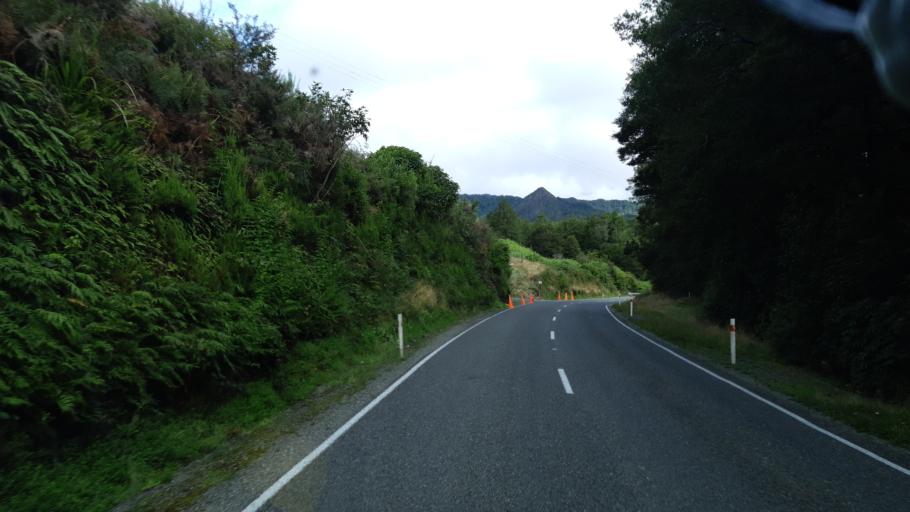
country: NZ
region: West Coast
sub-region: Buller District
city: Westport
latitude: -41.9846
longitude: 172.2071
